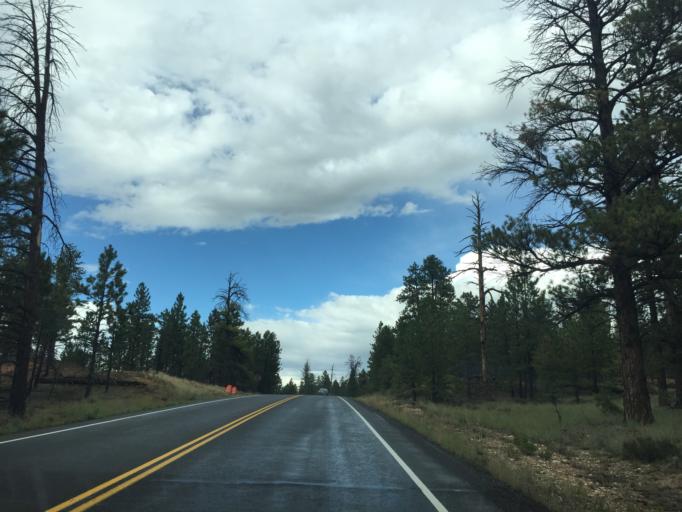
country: US
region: Utah
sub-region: Garfield County
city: Panguitch
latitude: 37.6434
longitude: -112.1675
